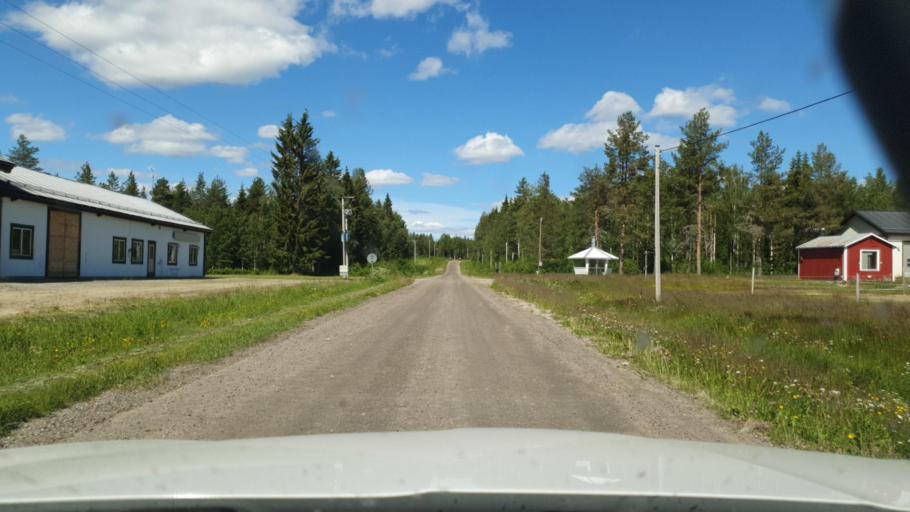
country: SE
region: Vaesterbotten
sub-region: Skelleftea Kommun
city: Backa
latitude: 65.1503
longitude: 21.1641
